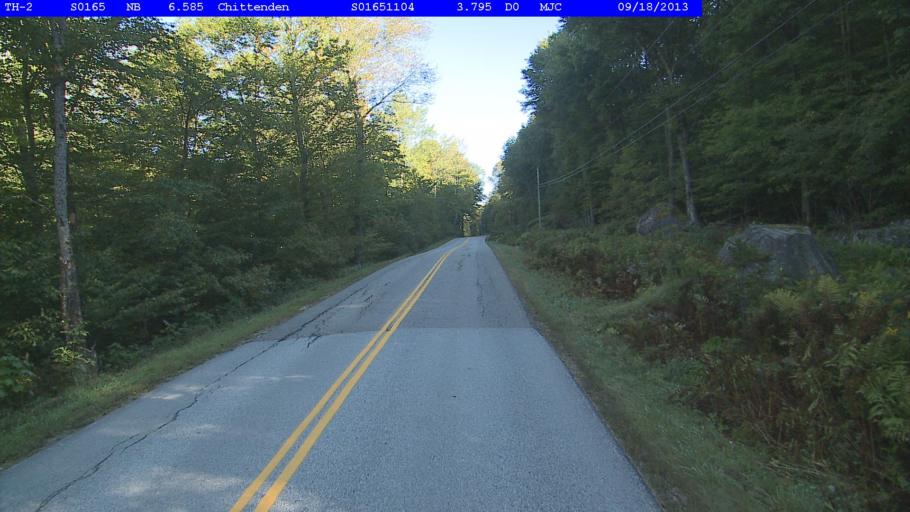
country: US
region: Vermont
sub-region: Rutland County
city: Rutland
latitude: 43.7287
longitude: -72.9708
